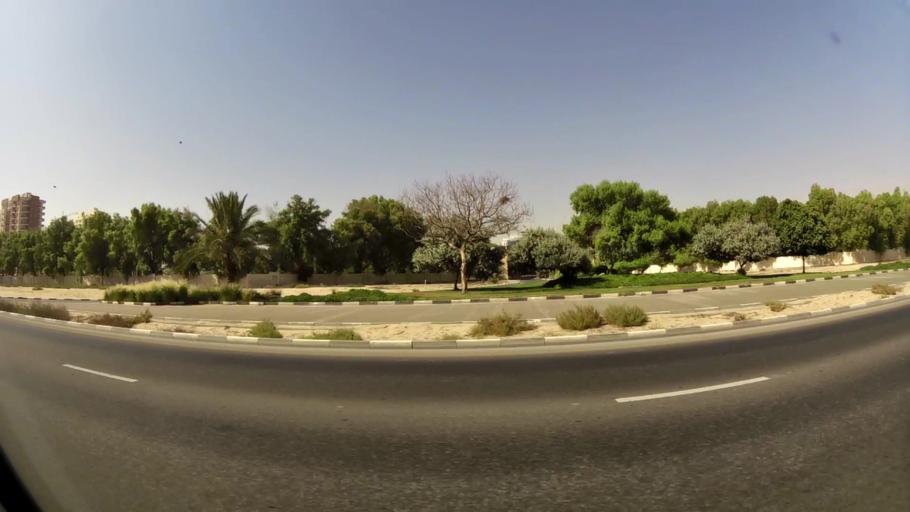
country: AE
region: Ash Shariqah
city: Sharjah
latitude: 25.2844
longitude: 55.3732
